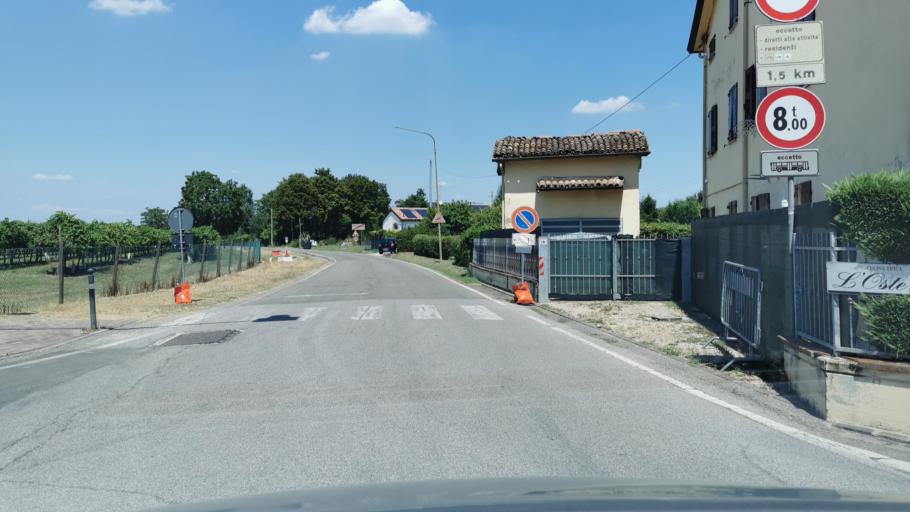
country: IT
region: Emilia-Romagna
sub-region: Provincia di Modena
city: Fossoli
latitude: 44.8192
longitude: 10.8975
